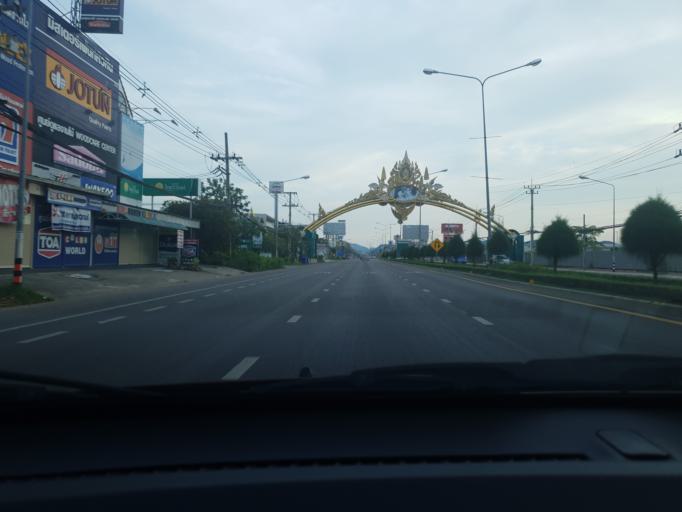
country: TH
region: Prachuap Khiri Khan
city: Hua Hin
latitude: 12.6217
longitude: 99.9507
